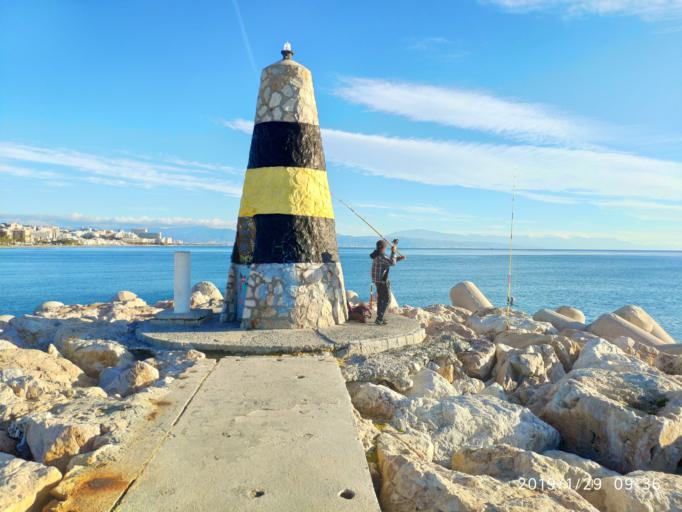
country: ES
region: Andalusia
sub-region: Provincia de Malaga
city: Torremolinos
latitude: 36.5975
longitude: -4.5079
